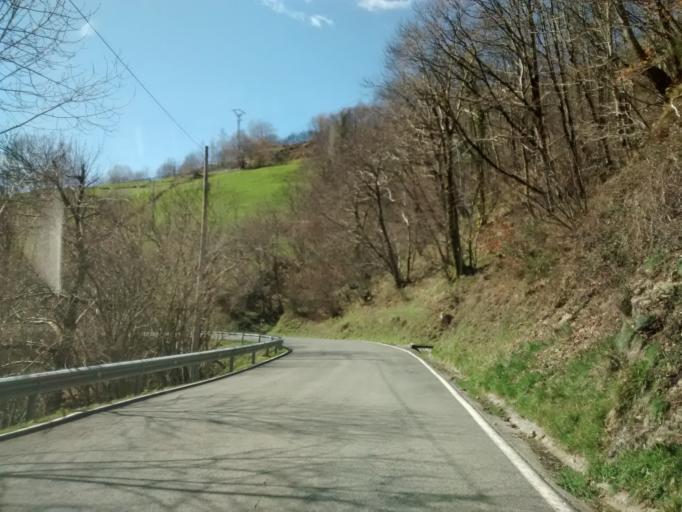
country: ES
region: Cantabria
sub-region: Provincia de Cantabria
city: Selaya
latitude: 43.2295
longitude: -3.7041
